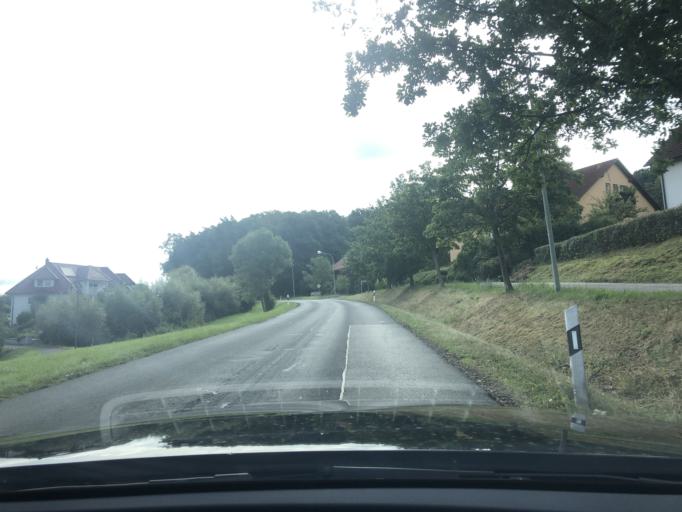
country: DE
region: Bavaria
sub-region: Regierungsbezirk Unterfranken
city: Rentweinsdorf
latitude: 50.0929
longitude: 10.8046
